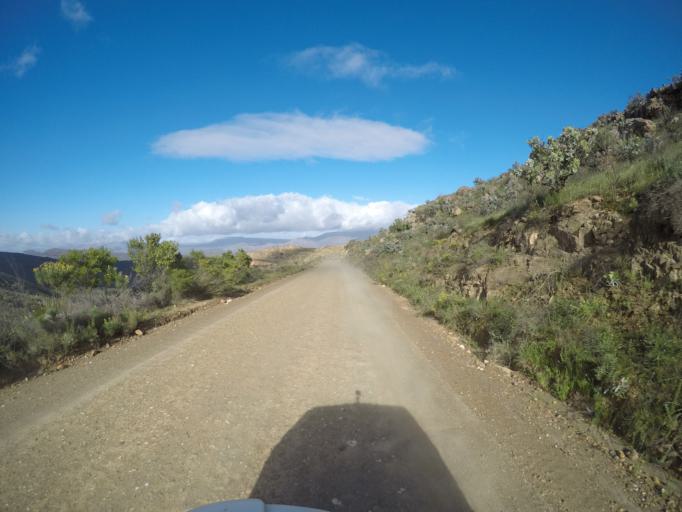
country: ZA
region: Western Cape
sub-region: West Coast District Municipality
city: Clanwilliam
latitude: -32.3479
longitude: 19.0118
